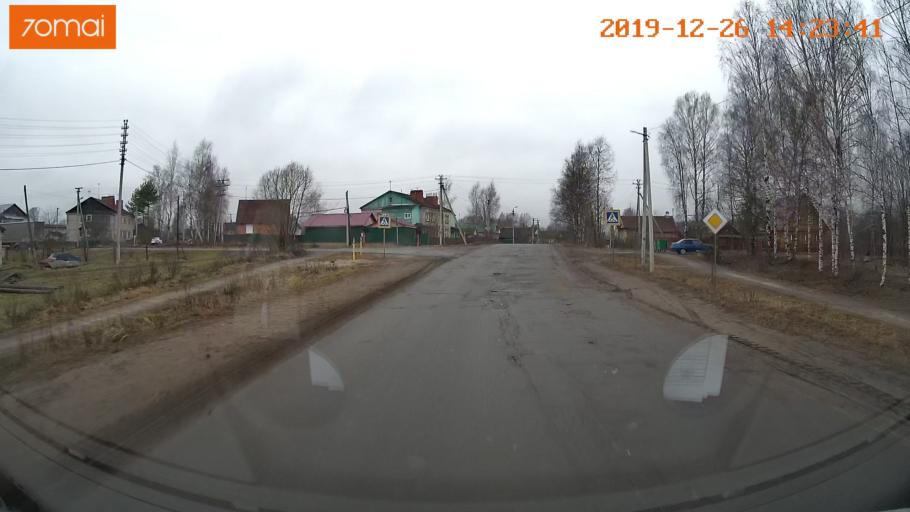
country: RU
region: Jaroslavl
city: Poshekhon'ye
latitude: 58.4978
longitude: 39.1142
